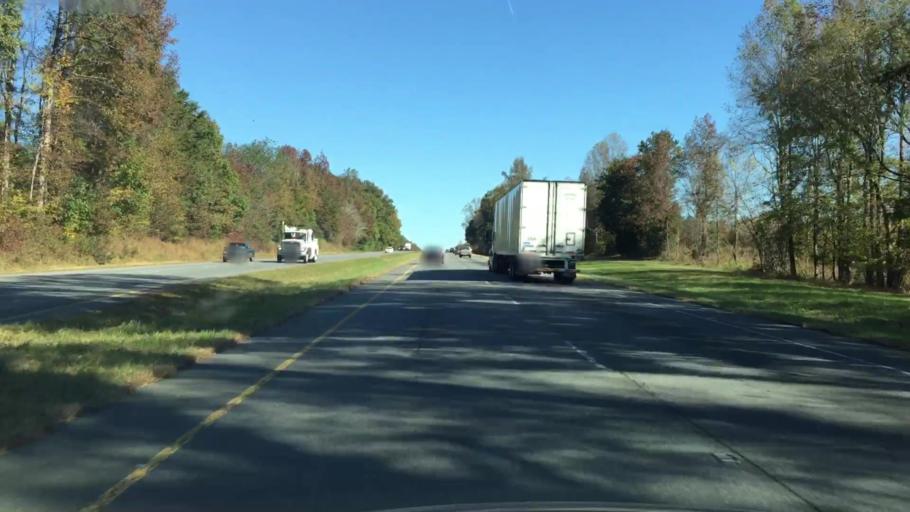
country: US
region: North Carolina
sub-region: Guilford County
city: McLeansville
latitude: 36.1933
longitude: -79.7010
